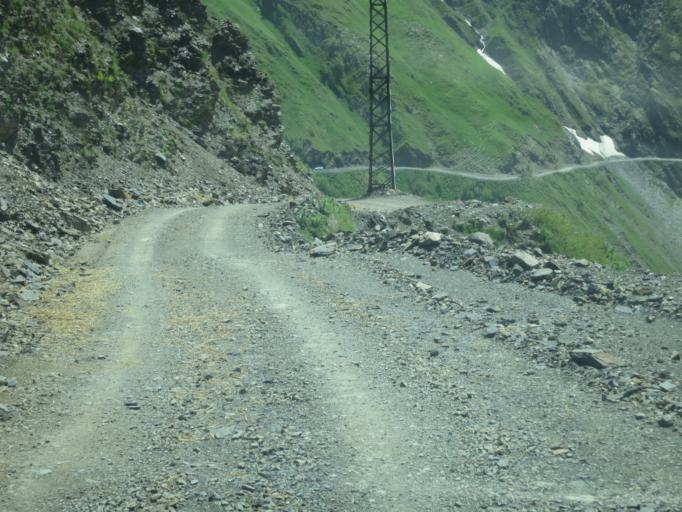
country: GE
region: Kakheti
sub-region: Telavi
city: Telavi
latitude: 42.2687
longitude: 45.4994
